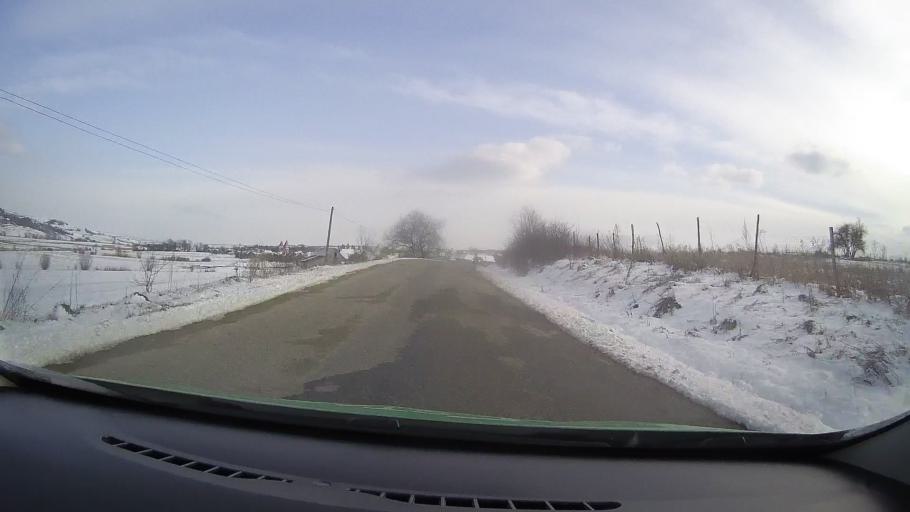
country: RO
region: Sibiu
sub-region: Comuna Merghindeal
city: Merghindeal
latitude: 45.9692
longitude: 24.7110
